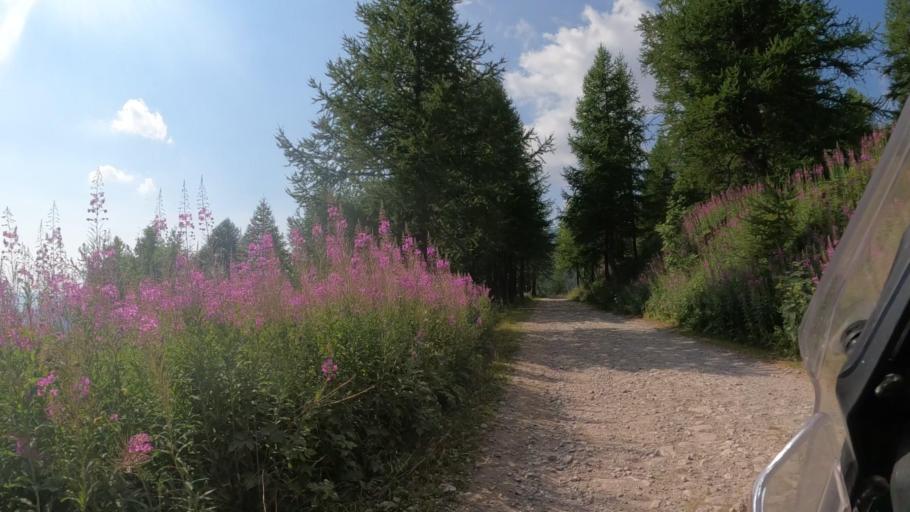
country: IT
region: Piedmont
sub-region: Provincia di Cuneo
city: Briga Alta
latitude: 44.1260
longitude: 7.6919
